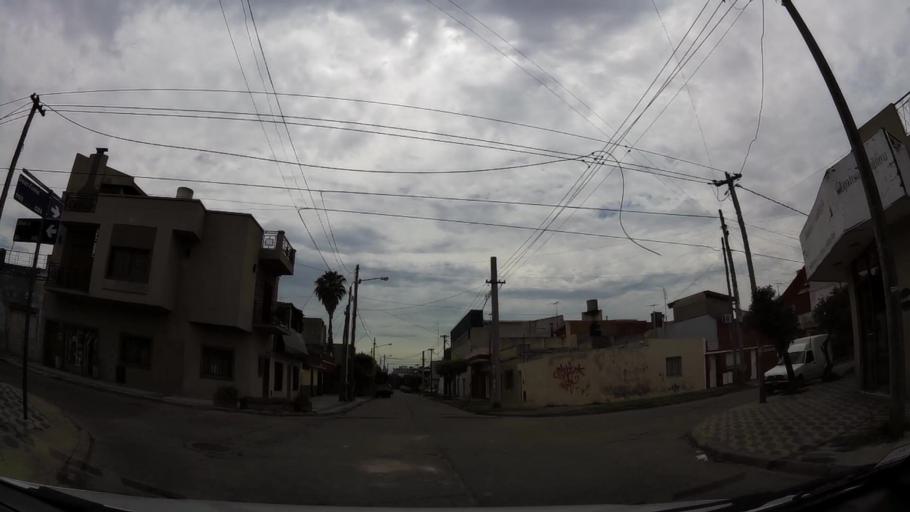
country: AR
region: Buenos Aires F.D.
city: Villa Lugano
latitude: -34.6836
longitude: -58.5093
